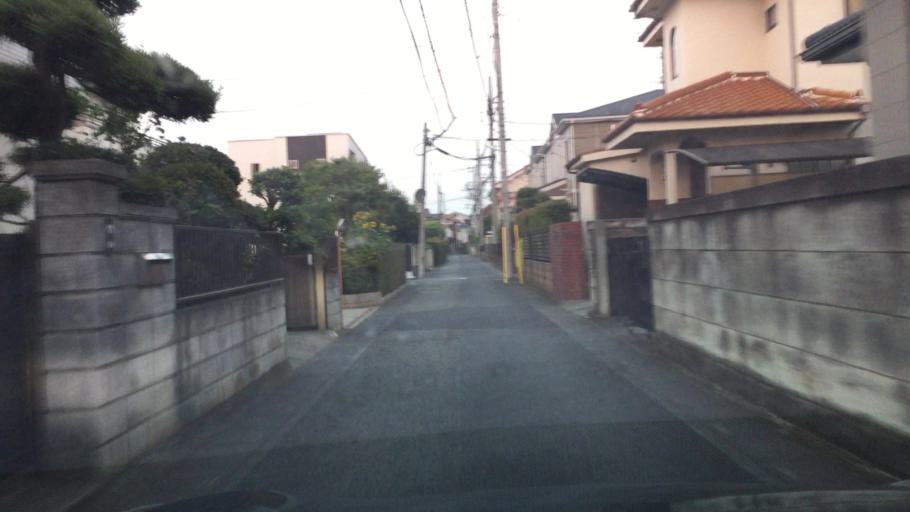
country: JP
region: Saitama
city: Ageoshimo
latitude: 35.9348
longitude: 139.6032
